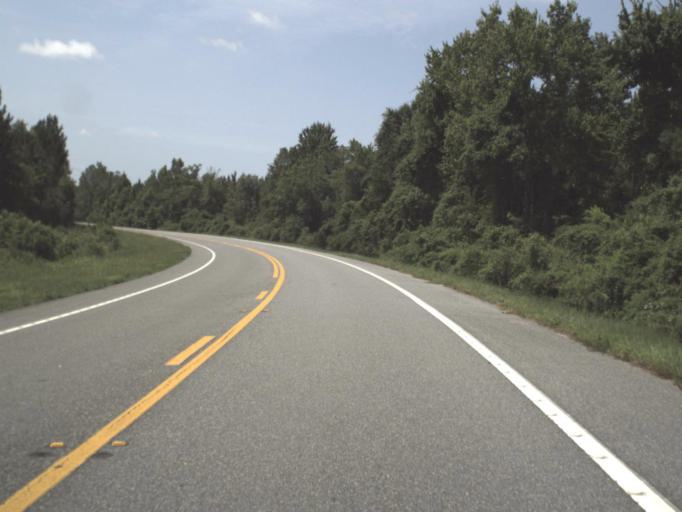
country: US
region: Florida
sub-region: Taylor County
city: Steinhatchee
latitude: 29.7281
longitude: -83.3610
